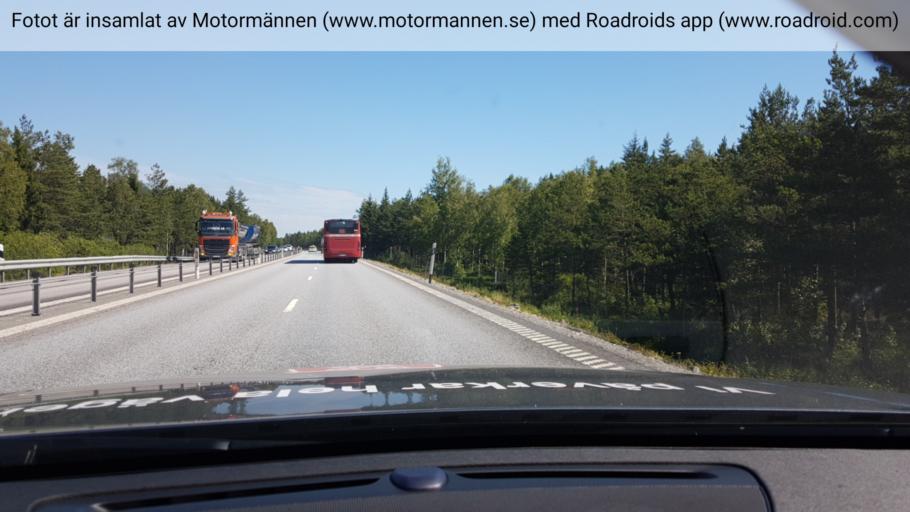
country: SE
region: Stockholm
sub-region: Osterakers Kommun
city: Akersberga
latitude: 59.5972
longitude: 18.2718
